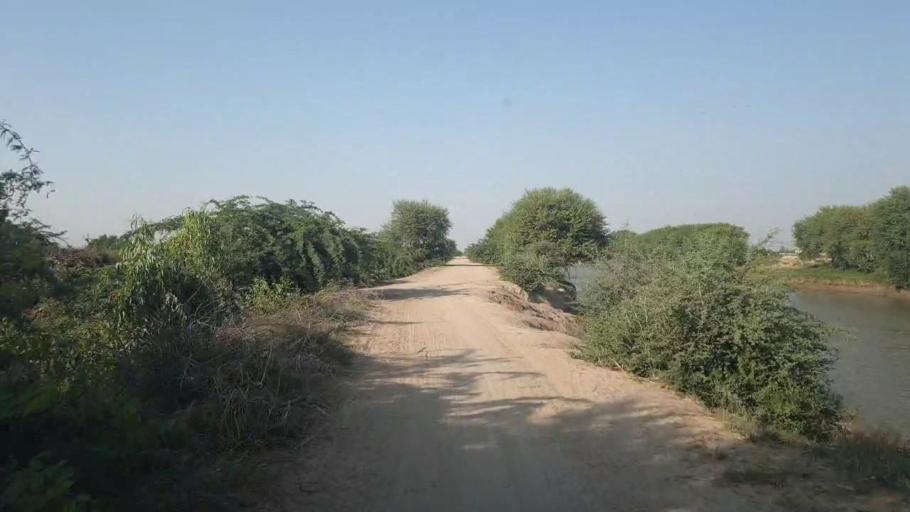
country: PK
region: Sindh
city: Badin
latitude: 24.6458
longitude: 68.8151
